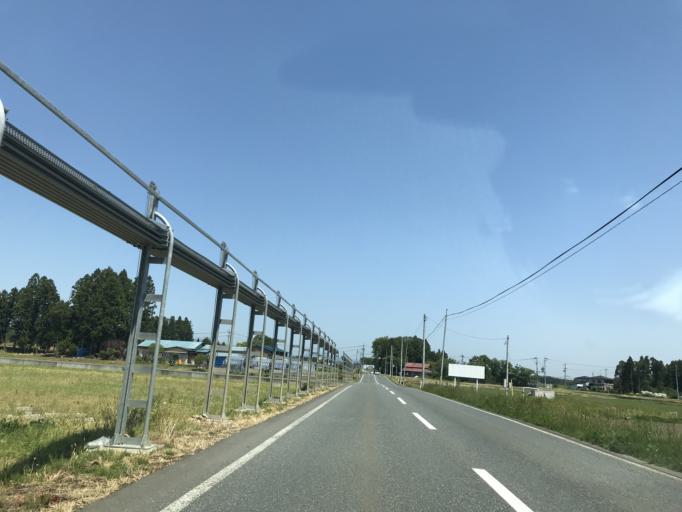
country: JP
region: Iwate
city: Kitakami
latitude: 39.2518
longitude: 141.0654
